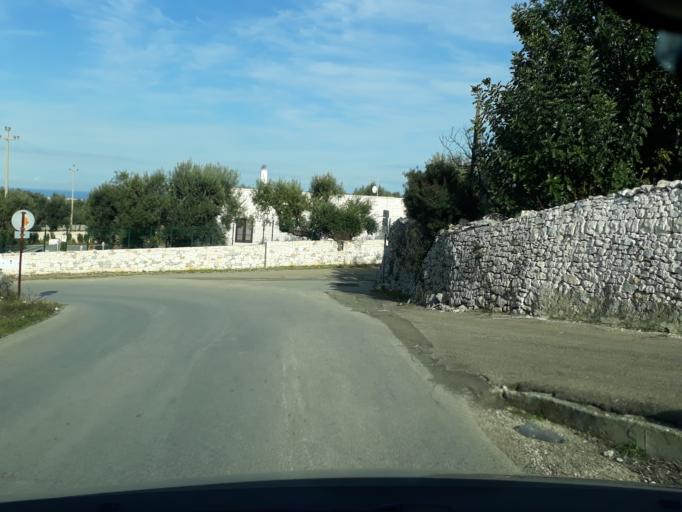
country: IT
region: Apulia
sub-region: Provincia di Brindisi
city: Fasano
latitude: 40.8169
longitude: 17.3570
